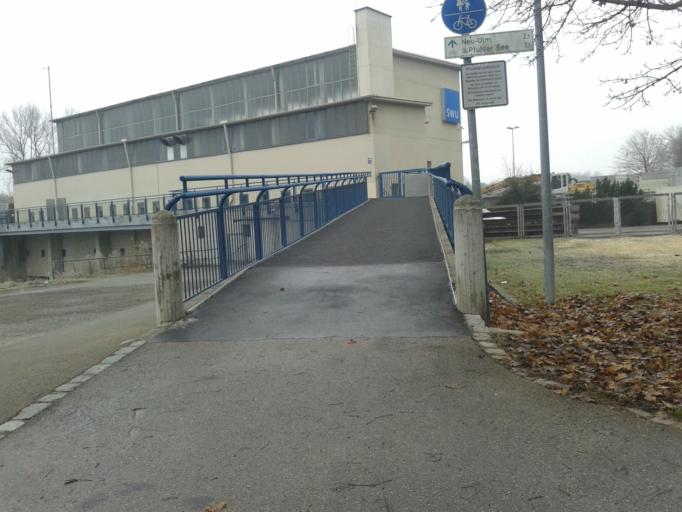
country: DE
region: Bavaria
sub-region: Swabia
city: Neu-Ulm
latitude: 48.4242
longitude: 10.0258
